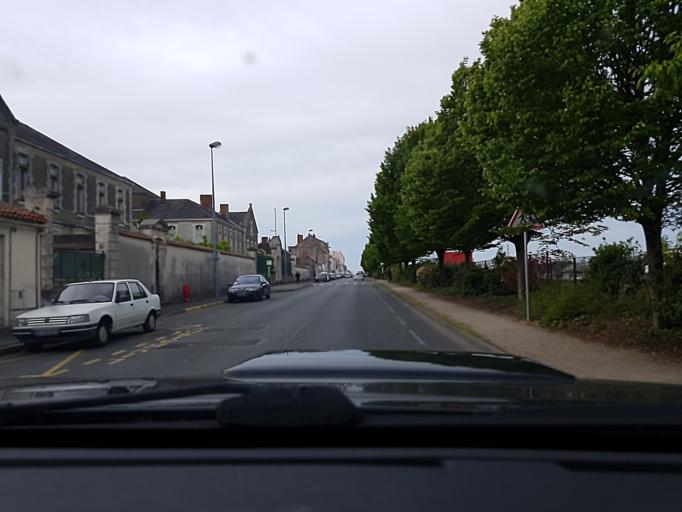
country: FR
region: Pays de la Loire
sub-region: Departement de la Vendee
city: La Roche-sur-Yon
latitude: 46.6763
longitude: -1.4353
